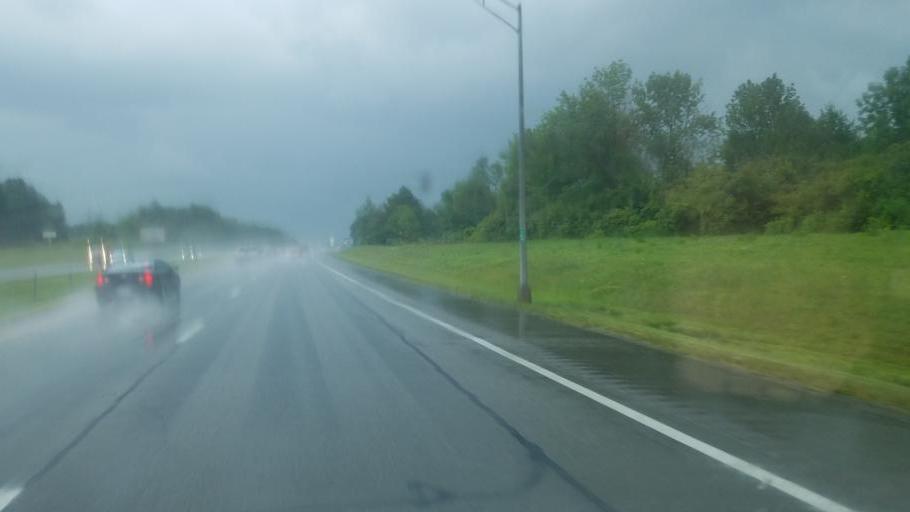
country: US
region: Ohio
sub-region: Trumbull County
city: Morgandale
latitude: 41.2769
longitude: -80.7952
